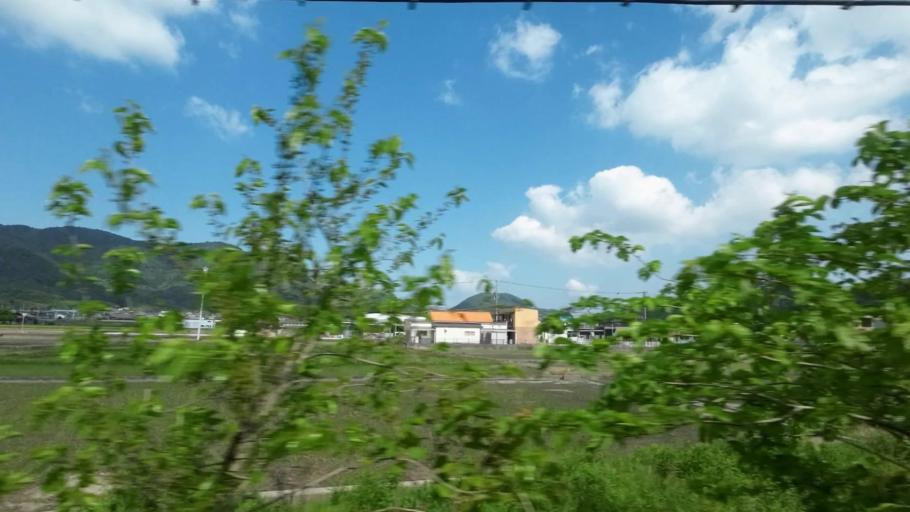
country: JP
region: Kagawa
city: Kan'onjicho
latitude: 34.1769
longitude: 133.6943
